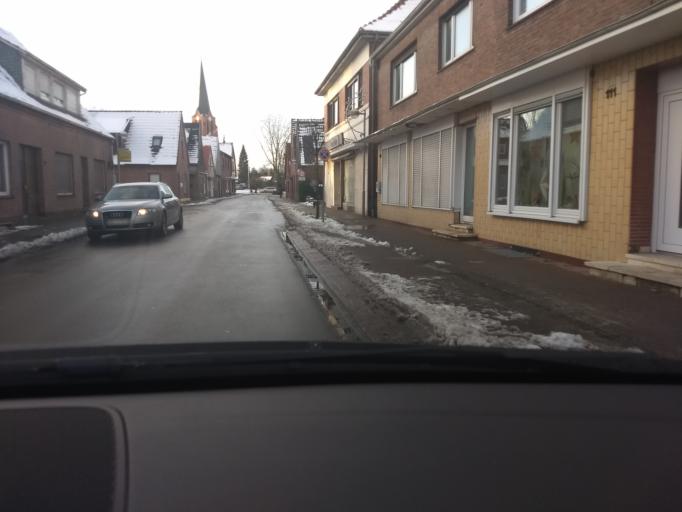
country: DE
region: Lower Saxony
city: Lage
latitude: 52.4962
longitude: 6.9715
